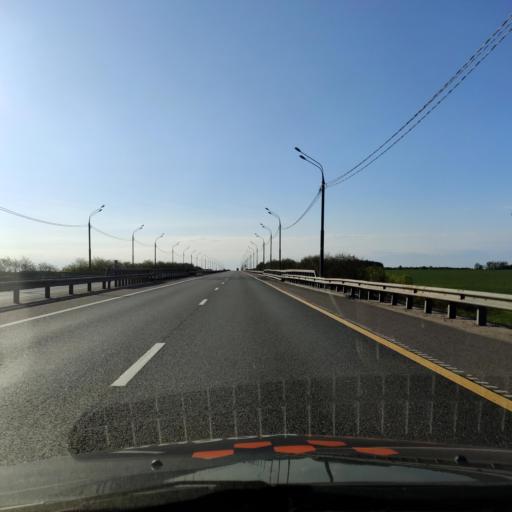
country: RU
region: Lipetsk
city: Khlevnoye
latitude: 52.2368
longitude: 39.0765
